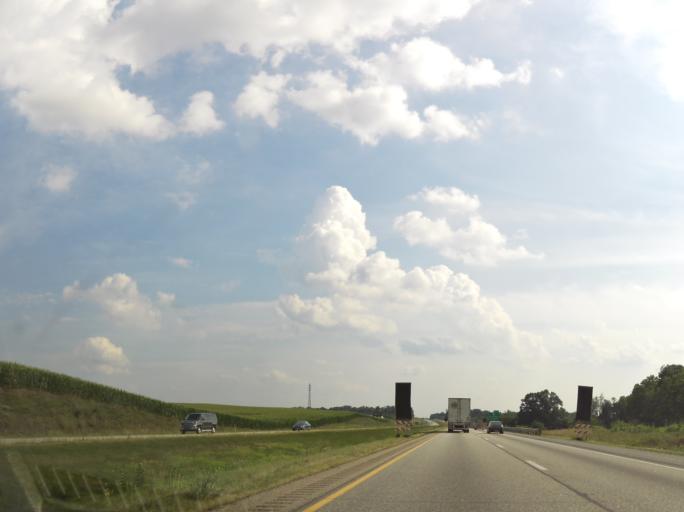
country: US
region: Pennsylvania
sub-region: Franklin County
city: Greencastle
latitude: 39.8035
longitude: -77.7079
